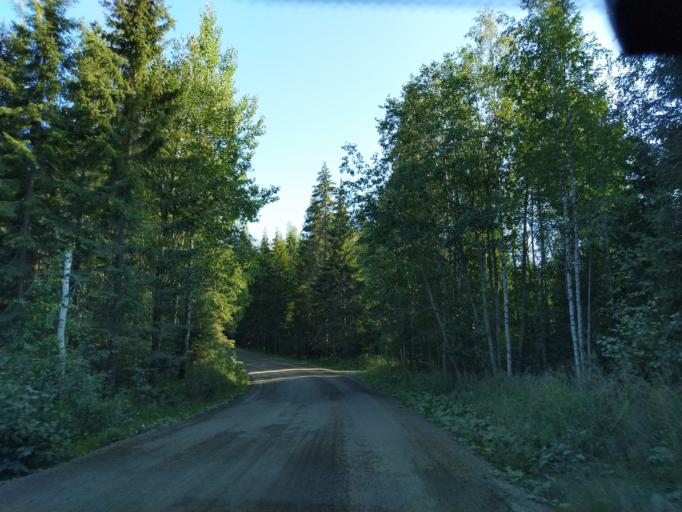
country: FI
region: Central Finland
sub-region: Jaemsae
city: Kuhmoinen
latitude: 61.6271
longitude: 25.0927
